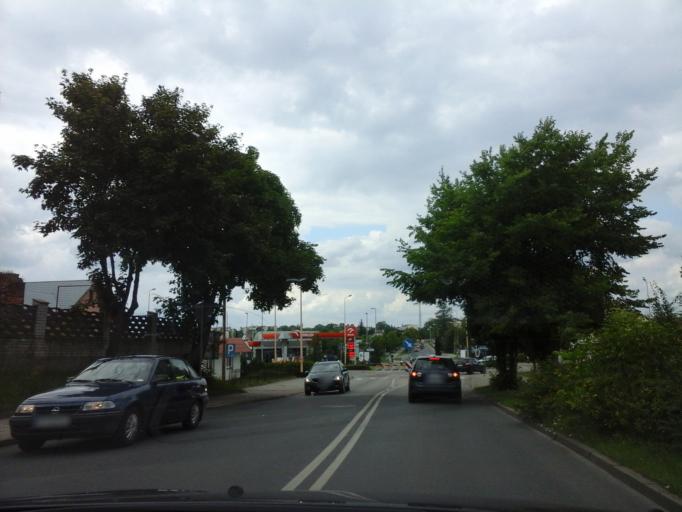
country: PL
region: West Pomeranian Voivodeship
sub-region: Powiat choszczenski
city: Choszczno
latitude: 53.1697
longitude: 15.4195
